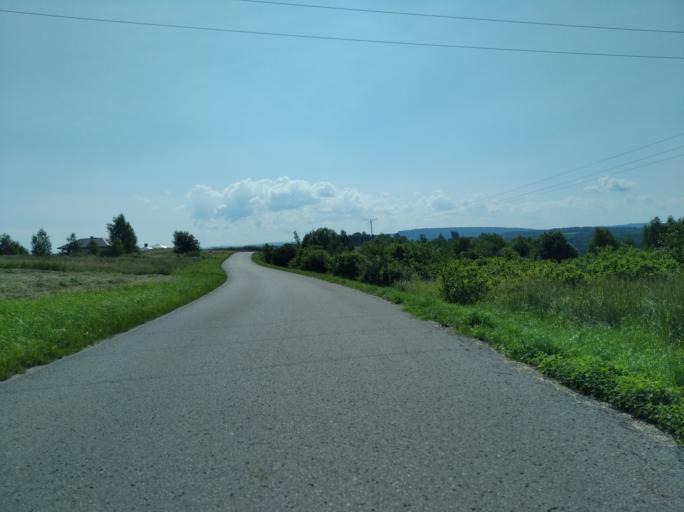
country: PL
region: Subcarpathian Voivodeship
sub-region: Powiat rzeszowski
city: Dynow
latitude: 49.8142
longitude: 22.2029
